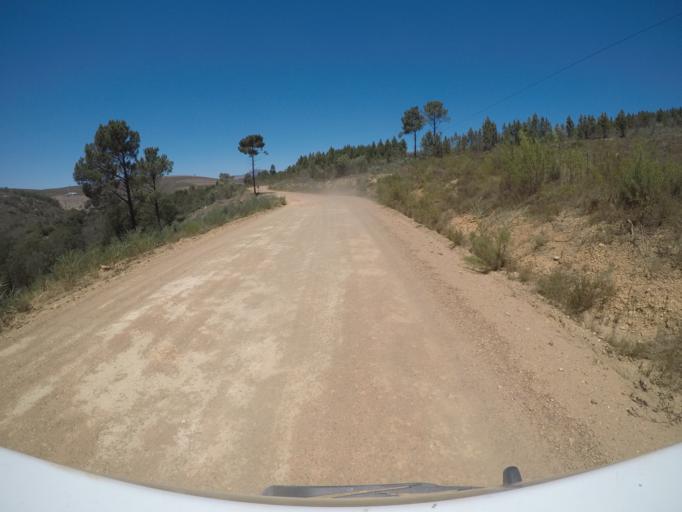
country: ZA
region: Western Cape
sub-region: Overberg District Municipality
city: Caledon
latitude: -34.1842
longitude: 19.2228
